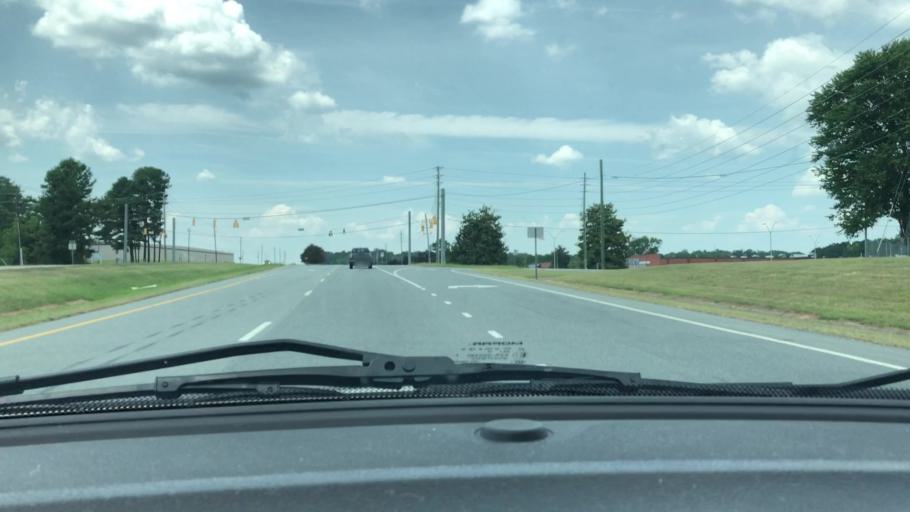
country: US
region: North Carolina
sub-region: Lee County
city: Sanford
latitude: 35.5118
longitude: -79.2126
